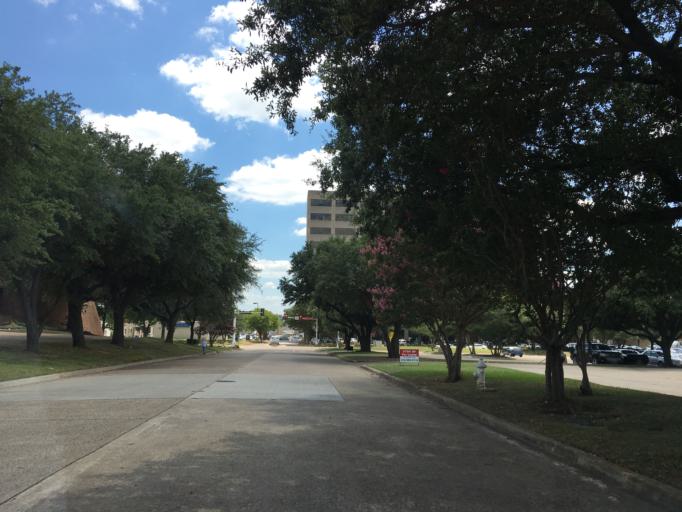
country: US
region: Texas
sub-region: Dallas County
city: Addison
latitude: 32.9410
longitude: -96.8368
